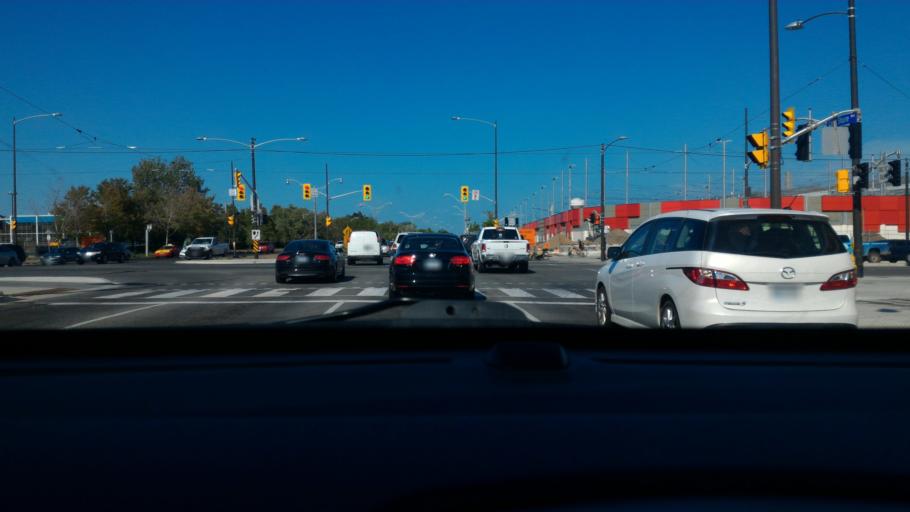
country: CA
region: Ontario
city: Toronto
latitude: 43.6588
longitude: -79.3288
